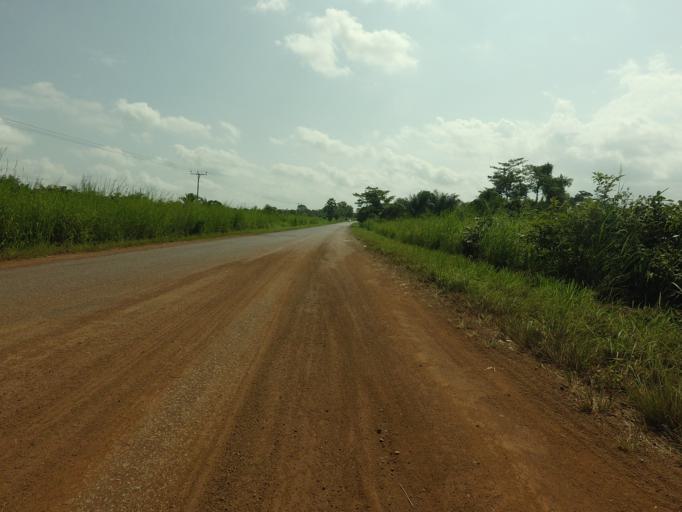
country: GH
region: Volta
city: Ho
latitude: 6.3936
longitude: 0.8027
